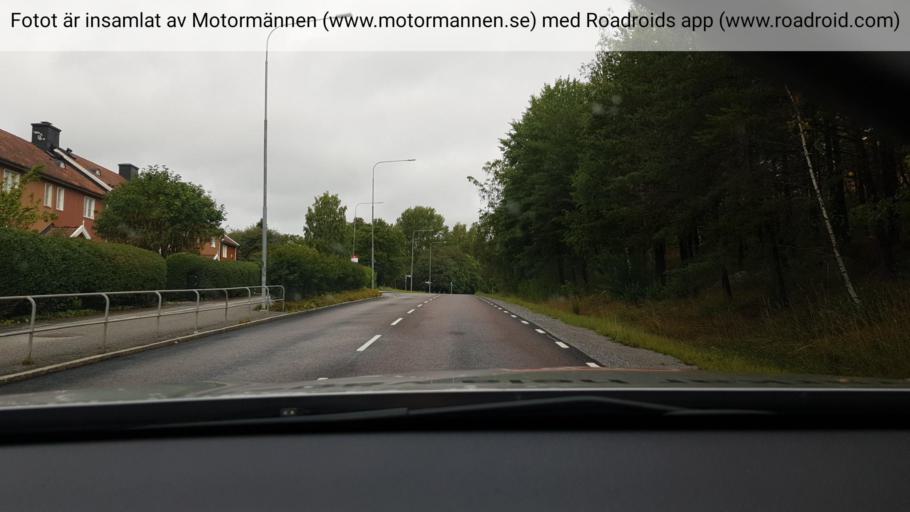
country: SE
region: Stockholm
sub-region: Lidingo
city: Brevik
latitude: 59.3500
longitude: 18.1684
